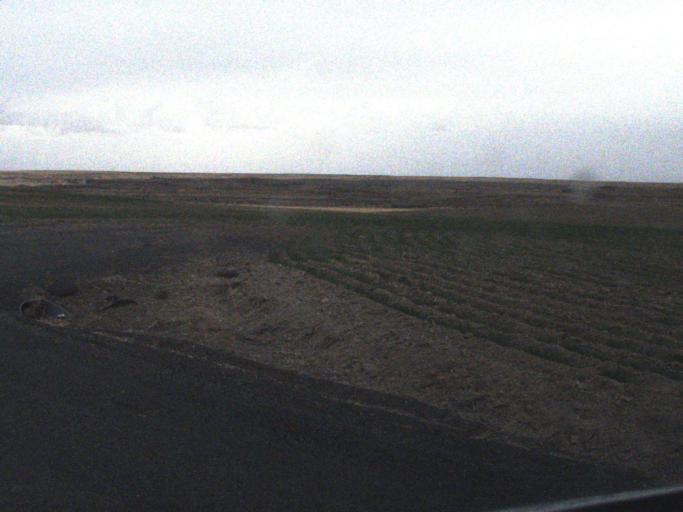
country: US
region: Washington
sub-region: Franklin County
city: Connell
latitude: 46.7950
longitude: -118.5368
